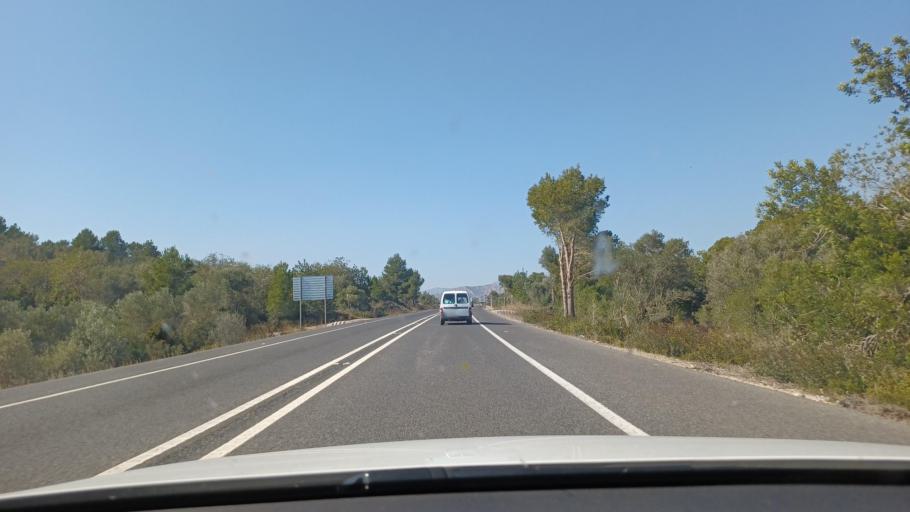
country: ES
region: Catalonia
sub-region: Provincia de Tarragona
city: l'Ametlla de Mar
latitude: 40.8956
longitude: 0.7565
